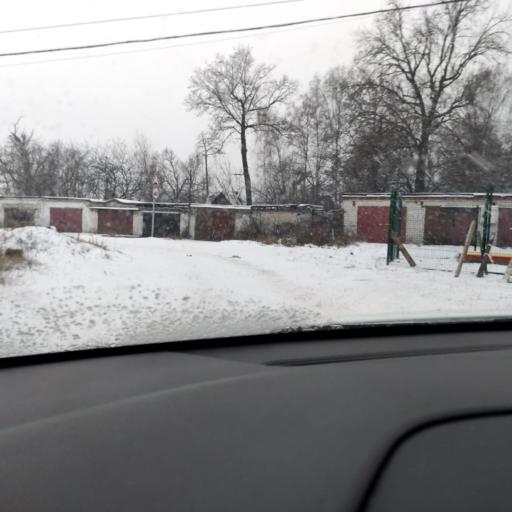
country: RU
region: Tatarstan
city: Staroye Arakchino
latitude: 55.8439
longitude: 49.0301
